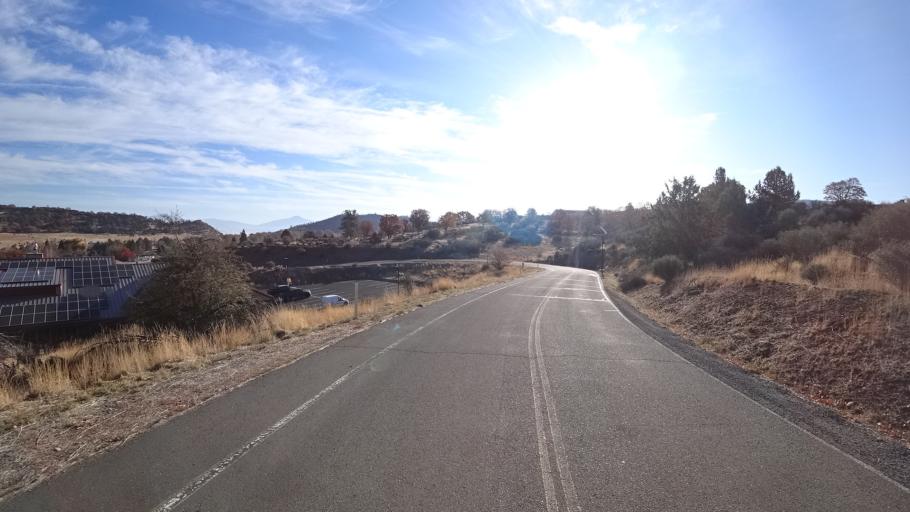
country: US
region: California
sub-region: Siskiyou County
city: Yreka
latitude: 41.7103
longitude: -122.6271
